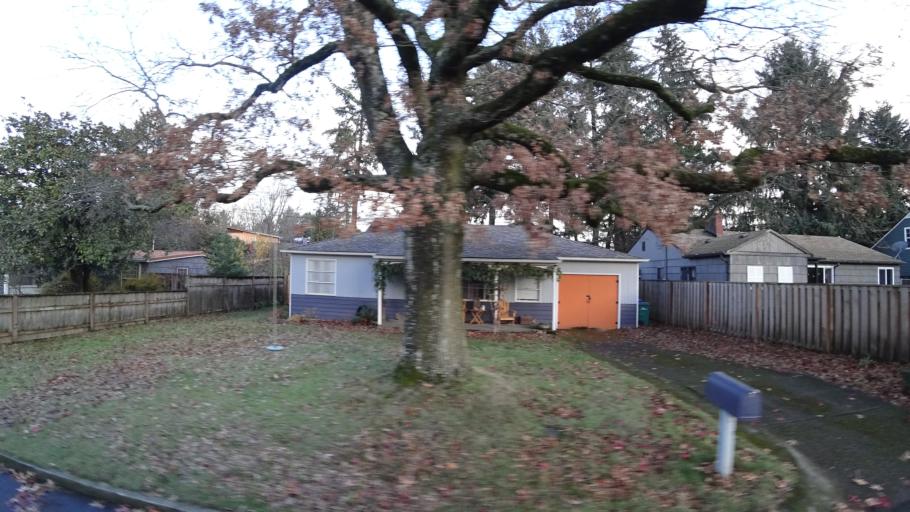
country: US
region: Oregon
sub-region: Multnomah County
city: Lents
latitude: 45.5152
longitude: -122.5471
